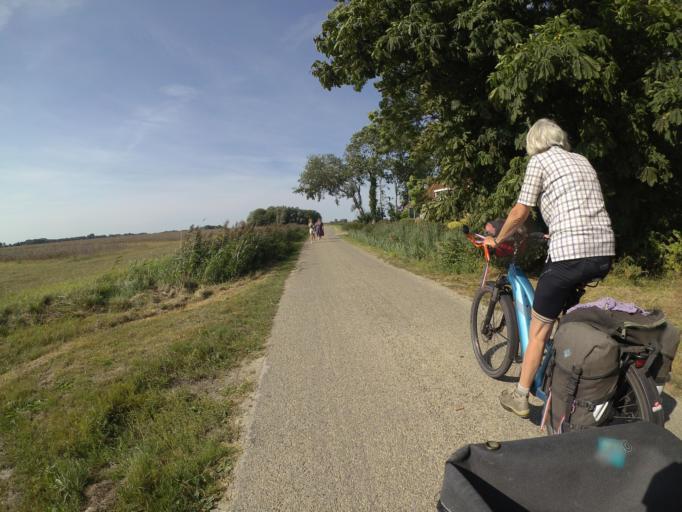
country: NL
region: Friesland
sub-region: Gemeente Ferwerderadiel
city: Ferwert
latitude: 53.3419
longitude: 5.8071
